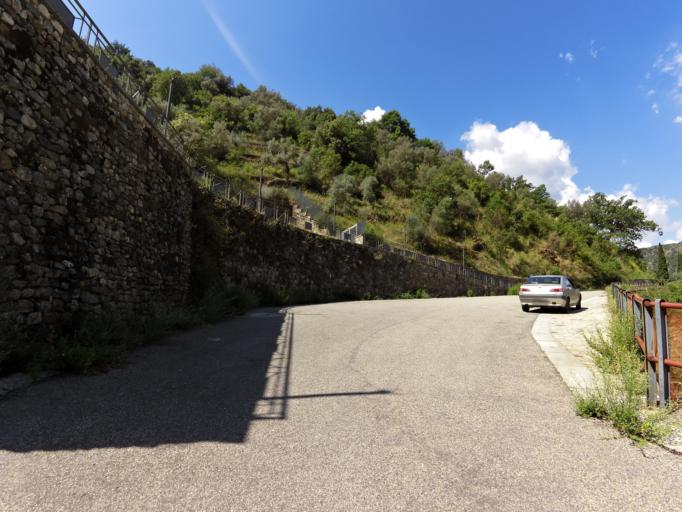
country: IT
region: Calabria
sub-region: Provincia di Reggio Calabria
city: Bivongi
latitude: 38.4846
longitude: 16.4609
